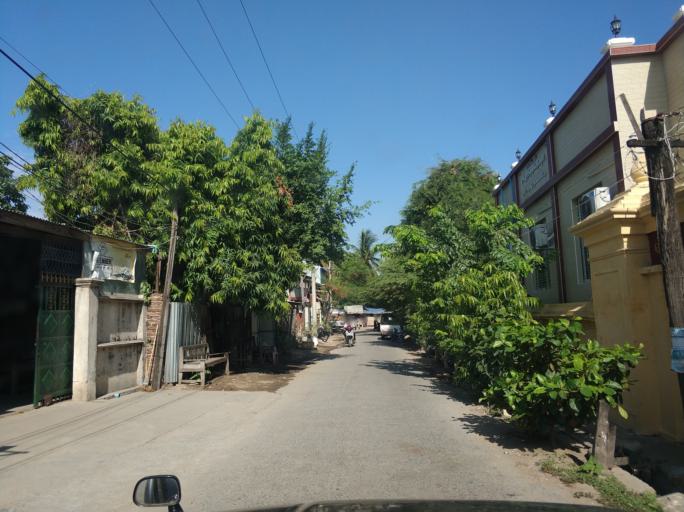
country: MM
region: Mandalay
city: Mandalay
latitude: 21.9718
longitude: 96.0694
